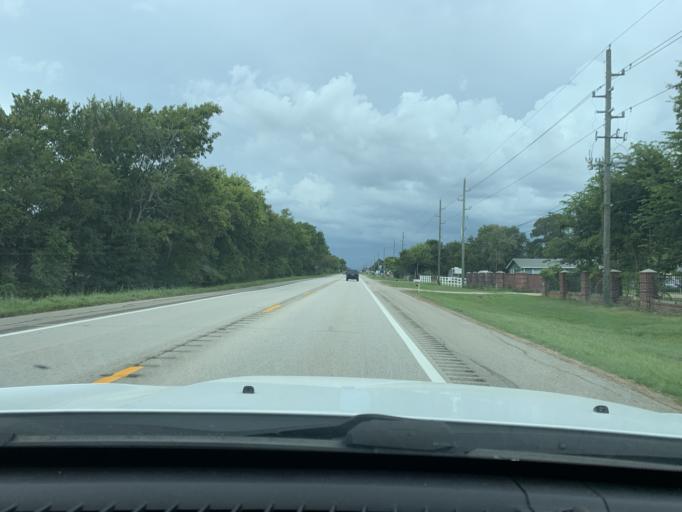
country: US
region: Texas
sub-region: Fort Bend County
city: Greatwood
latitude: 29.5394
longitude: -95.7162
